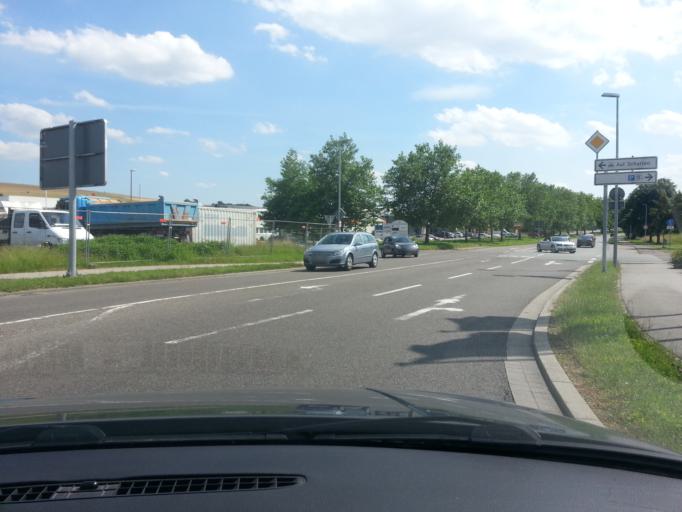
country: DE
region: Saarland
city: Blieskastel
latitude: 49.2357
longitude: 7.2702
